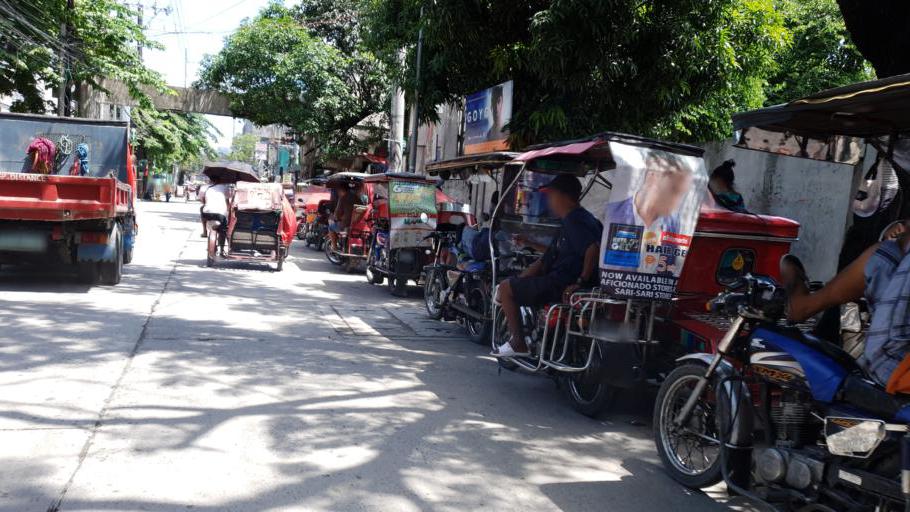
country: PH
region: Metro Manila
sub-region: City of Manila
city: Quiapo
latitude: 14.5994
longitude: 121.0047
